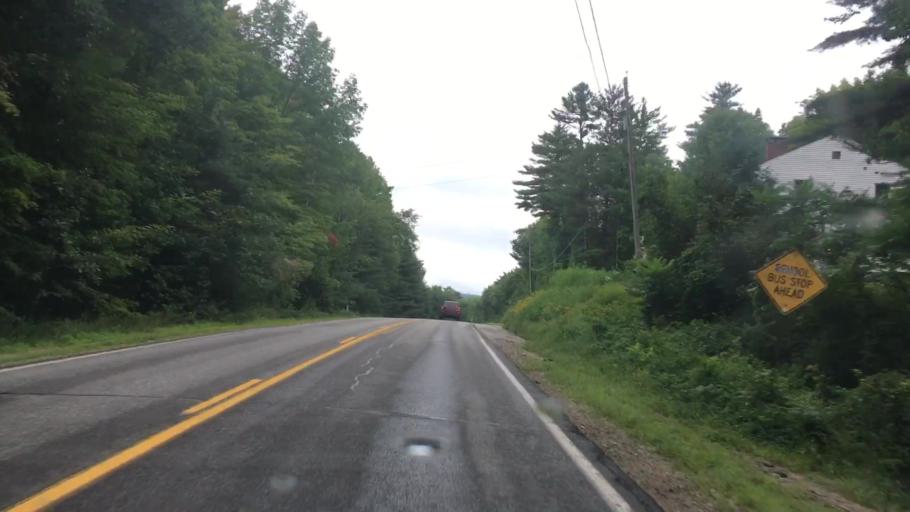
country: US
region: Maine
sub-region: Oxford County
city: Brownfield
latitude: 43.9554
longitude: -70.8970
